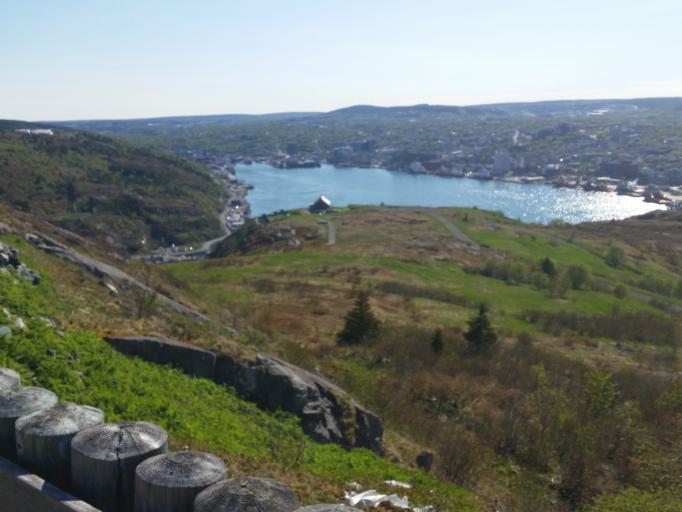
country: CA
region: Newfoundland and Labrador
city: St. John's
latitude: 47.5702
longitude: -52.6820
